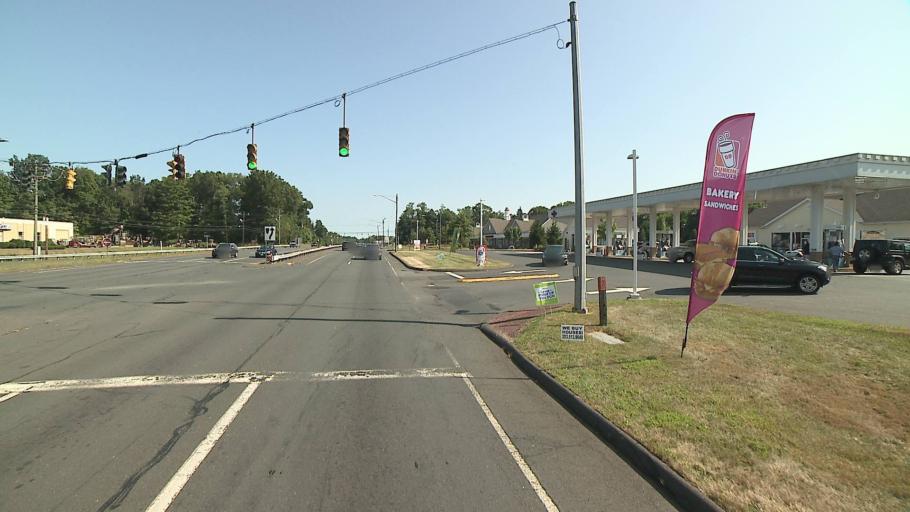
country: US
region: Connecticut
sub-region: Hartford County
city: Kensington
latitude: 41.5974
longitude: -72.7550
